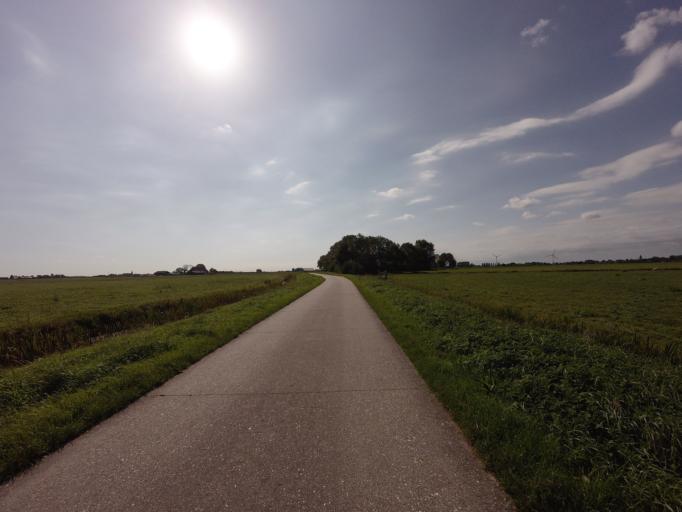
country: NL
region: Friesland
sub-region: Gemeente Littenseradiel
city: Makkum
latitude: 53.0947
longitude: 5.6448
